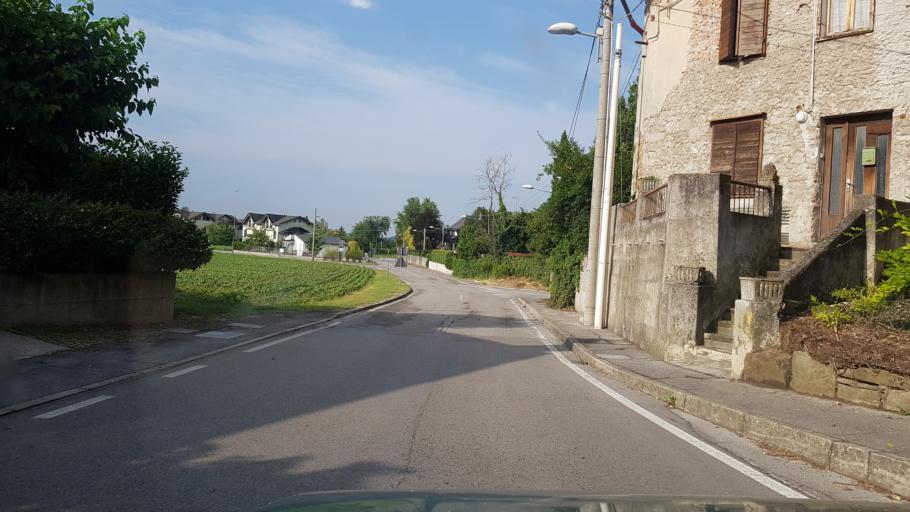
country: IT
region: Friuli Venezia Giulia
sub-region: Provincia di Gorizia
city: Mossa
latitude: 45.9380
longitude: 13.5428
